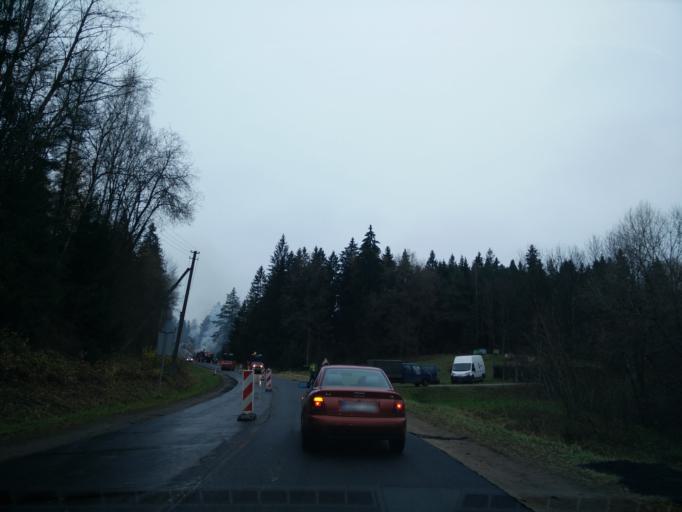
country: LT
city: Ariogala
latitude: 55.3017
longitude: 23.4388
